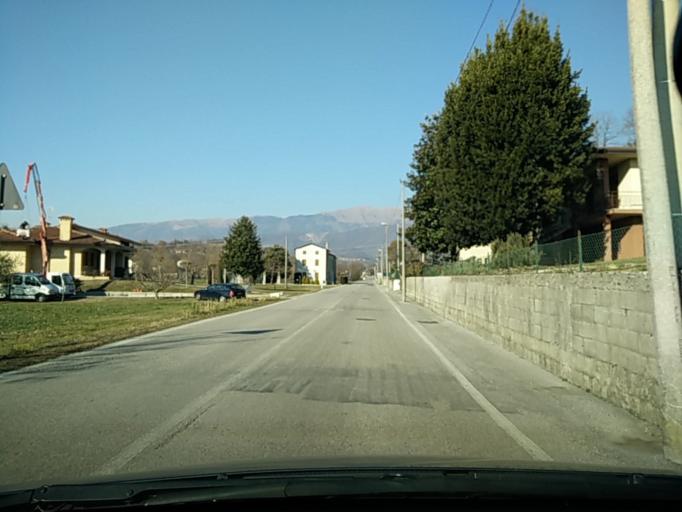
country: IT
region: Veneto
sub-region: Provincia di Treviso
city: Sarmede
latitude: 45.9781
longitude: 12.3806
